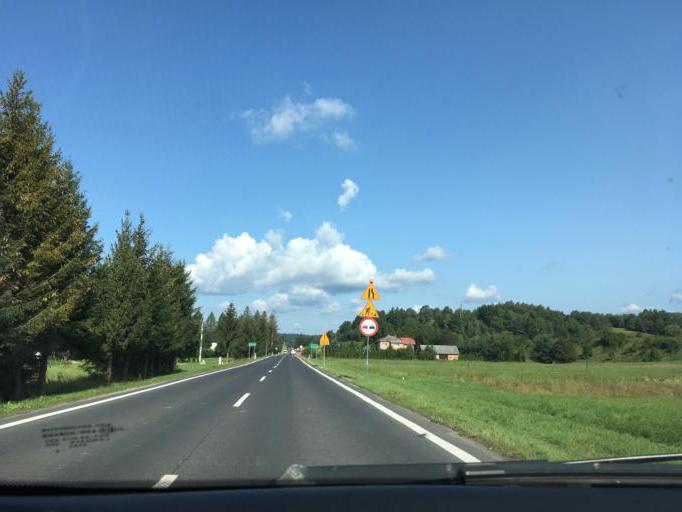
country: PL
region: Subcarpathian Voivodeship
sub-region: Powiat leski
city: Olszanica
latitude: 49.4671
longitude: 22.4646
